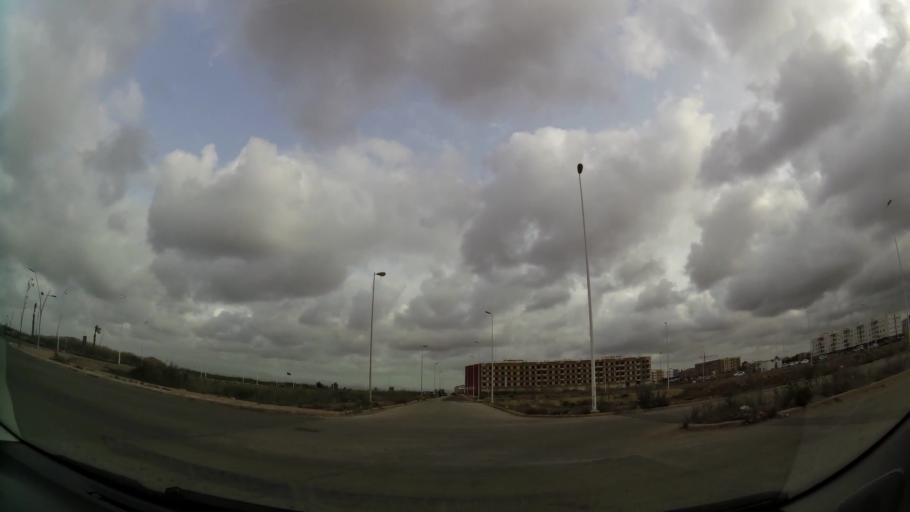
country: MA
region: Oriental
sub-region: Nador
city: Nador
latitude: 35.1574
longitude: -2.9081
